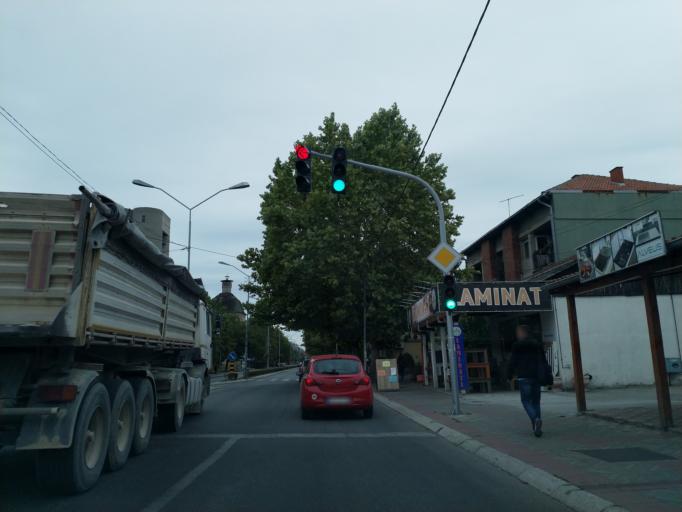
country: RS
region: Central Serbia
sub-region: Pomoravski Okrug
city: Jagodina
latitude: 43.9738
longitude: 21.2657
